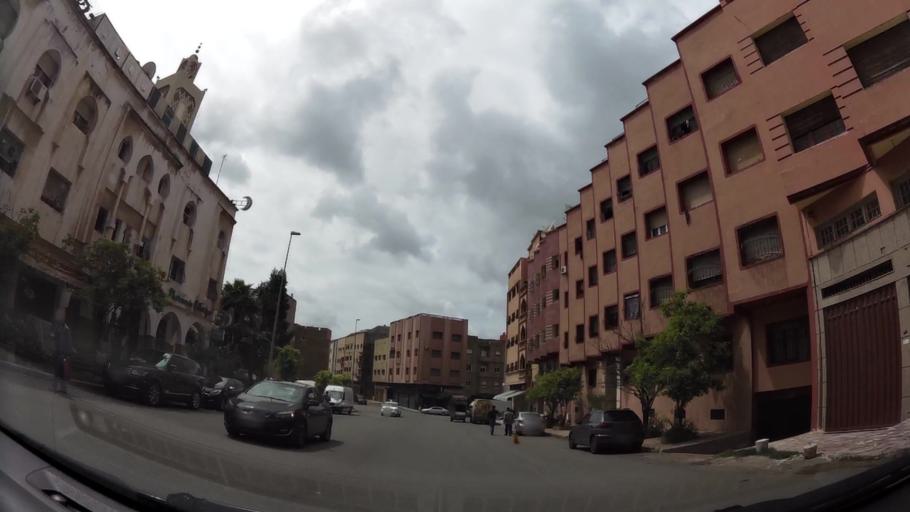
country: MA
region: Grand Casablanca
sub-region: Casablanca
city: Casablanca
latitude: 33.5335
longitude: -7.6080
